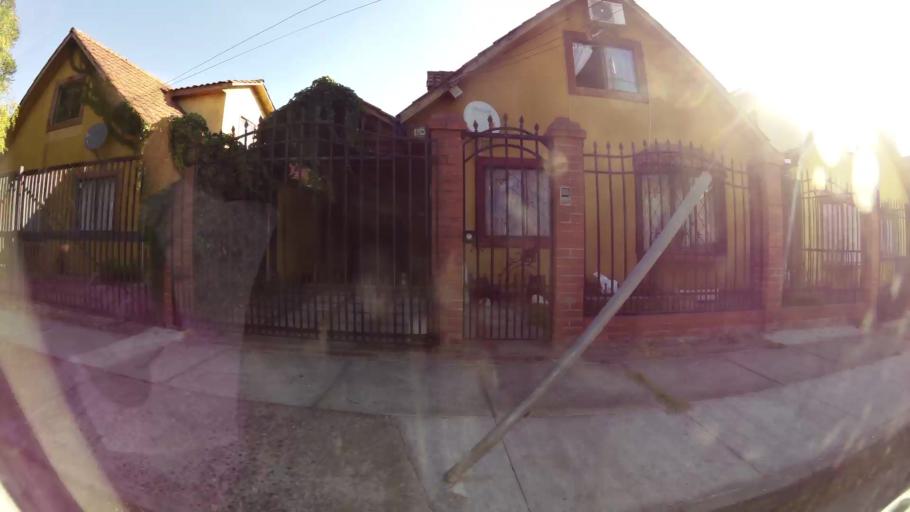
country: CL
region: Maule
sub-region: Provincia de Talca
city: Talca
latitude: -35.4422
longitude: -71.6880
